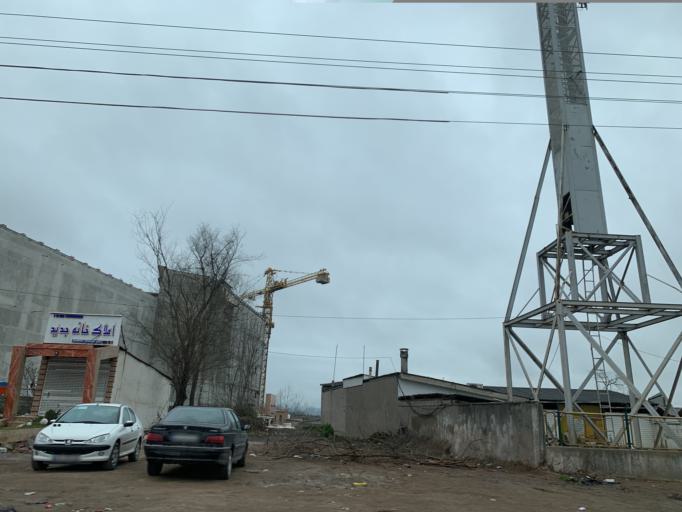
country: IR
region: Mazandaran
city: Amol
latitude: 36.4129
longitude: 52.3483
